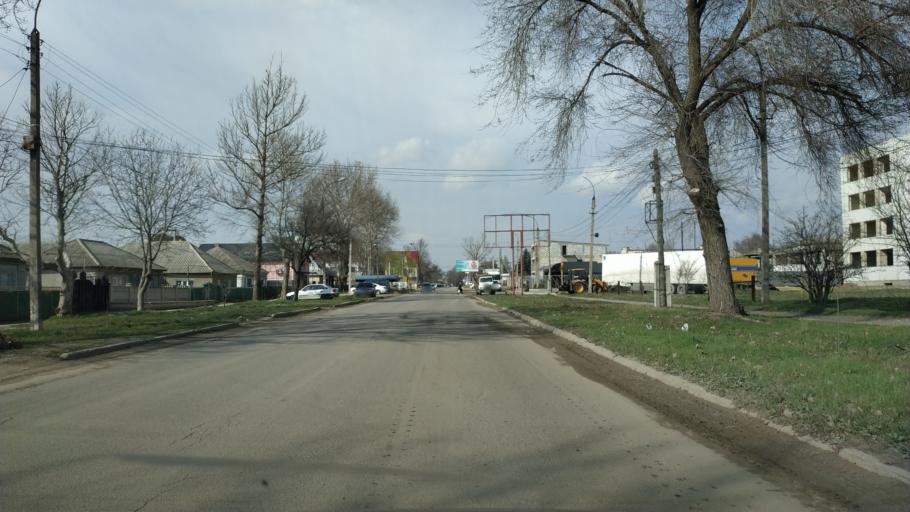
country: MD
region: Gagauzia
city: Vulcanesti
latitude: 45.6805
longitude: 28.4088
